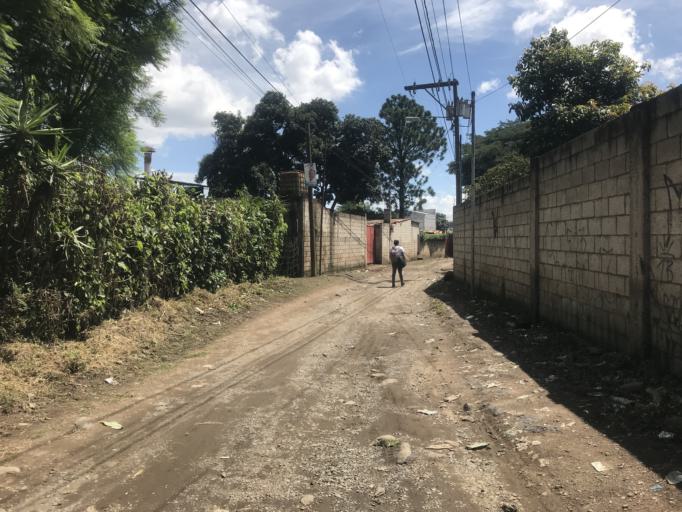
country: GT
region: Guatemala
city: Amatitlan
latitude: 14.4804
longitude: -90.6345
